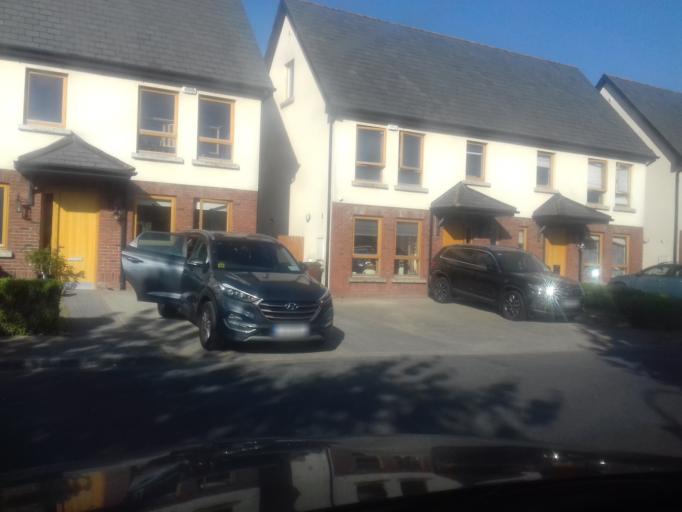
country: IE
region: Leinster
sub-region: Fingal County
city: Blanchardstown
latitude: 53.4337
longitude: -6.3761
